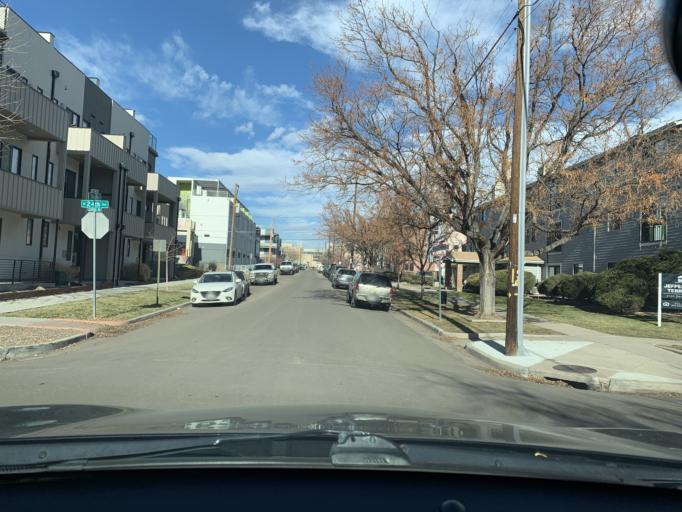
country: US
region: Colorado
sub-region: Denver County
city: Denver
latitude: 39.7524
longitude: -105.0221
